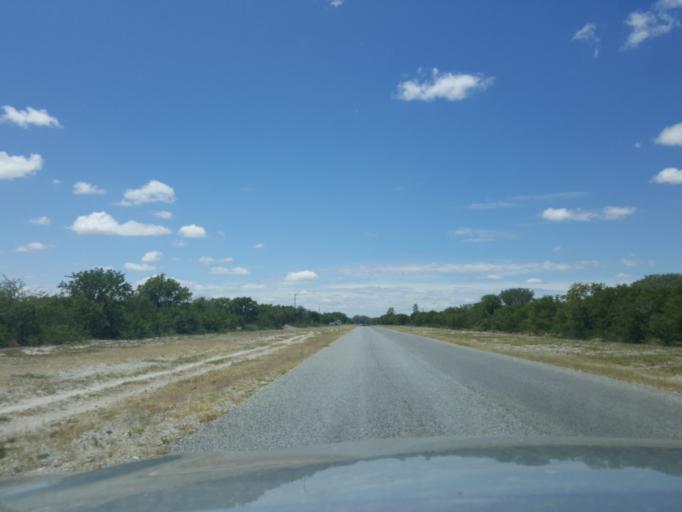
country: BW
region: Central
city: Nata
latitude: -20.2139
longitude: 26.1670
